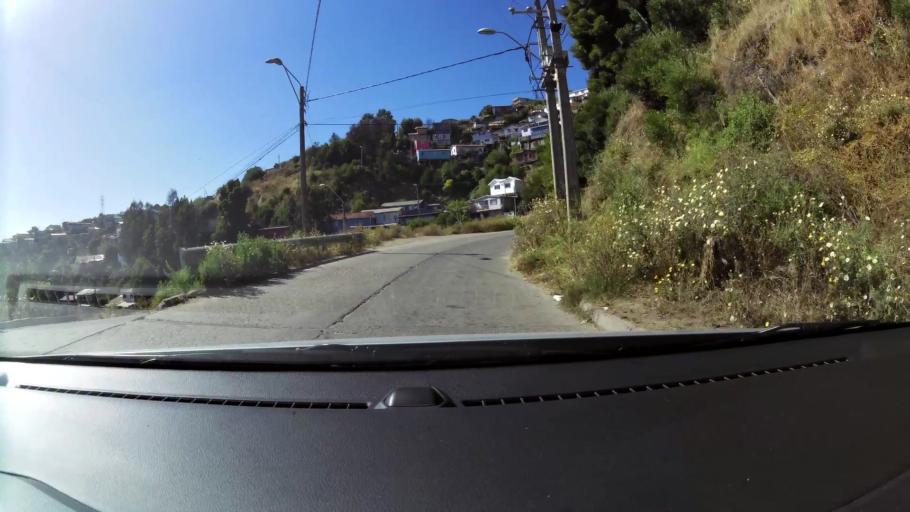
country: CL
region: Valparaiso
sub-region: Provincia de Valparaiso
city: Valparaiso
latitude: -33.0685
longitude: -71.5889
